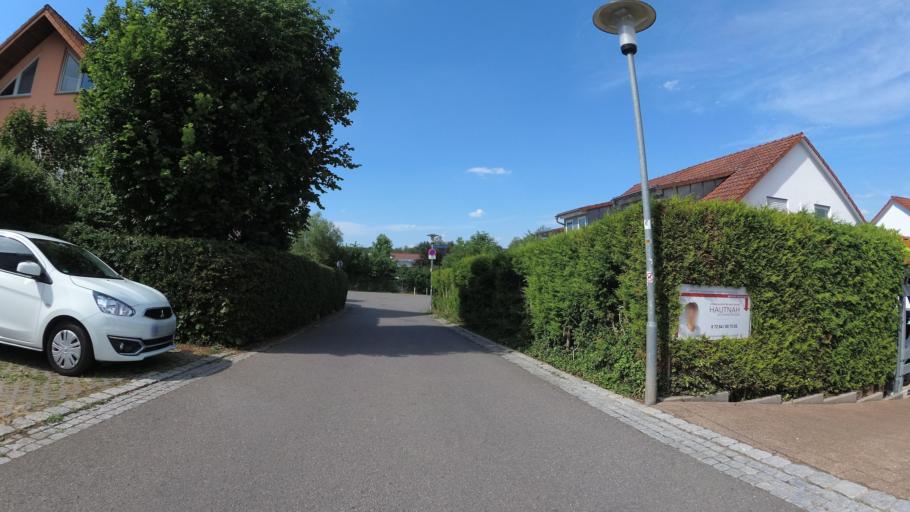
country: DE
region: Baden-Wuerttemberg
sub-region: Regierungsbezirk Stuttgart
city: Bad Rappenau
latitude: 49.2515
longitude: 9.1234
